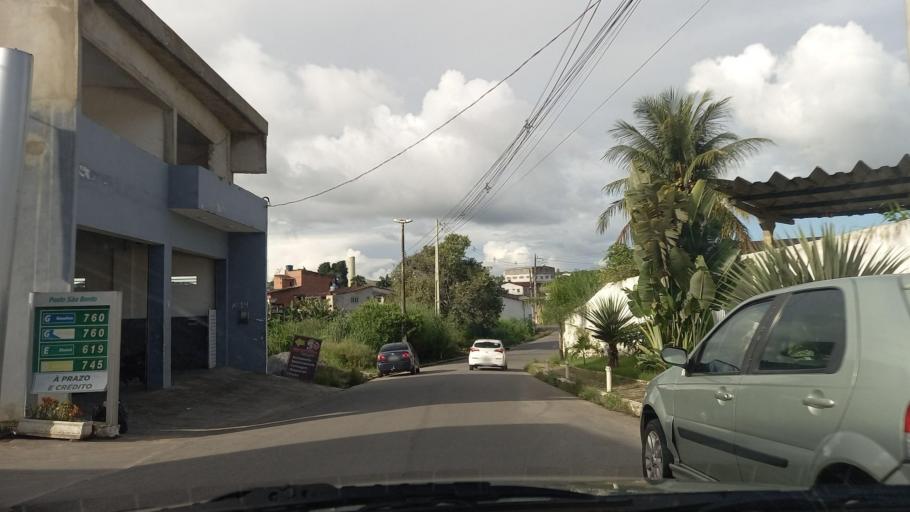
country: BR
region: Pernambuco
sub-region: Palmares
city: Palmares
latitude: -8.6786
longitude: -35.5806
